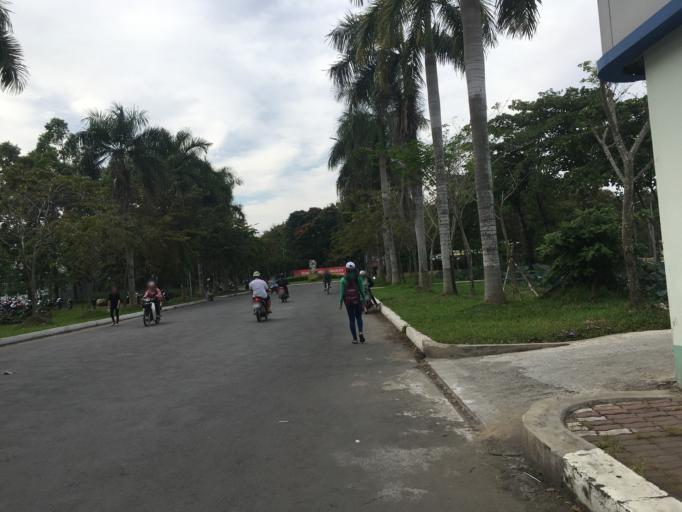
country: VN
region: Can Tho
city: Can Tho
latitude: 10.0307
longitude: 105.7715
